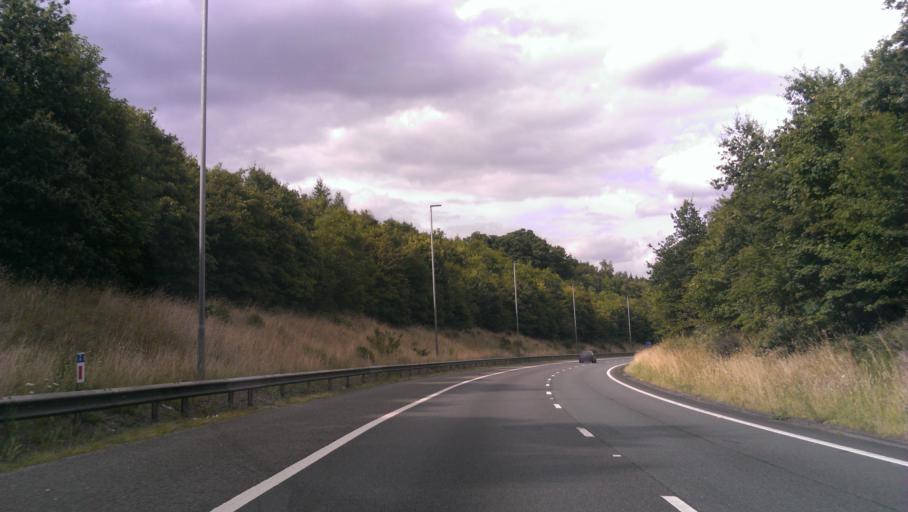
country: GB
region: England
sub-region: Kent
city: Swanley
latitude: 51.3925
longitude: 0.1960
